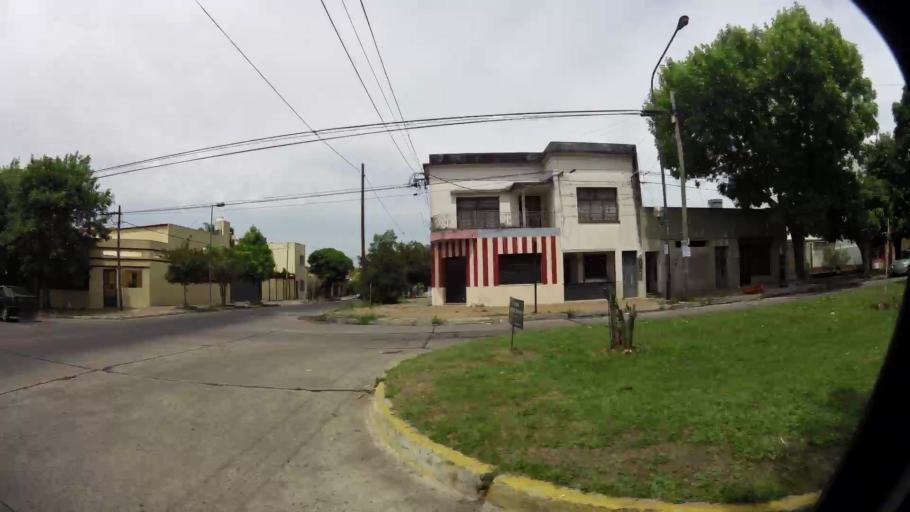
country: AR
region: Buenos Aires
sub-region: Partido de La Plata
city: La Plata
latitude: -34.9467
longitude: -57.9576
